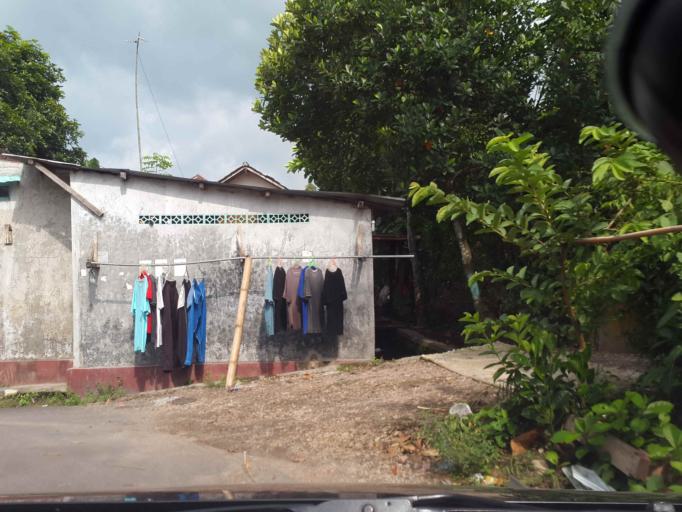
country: ID
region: West Nusa Tenggara
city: Kediri
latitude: -8.6523
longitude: 116.1343
